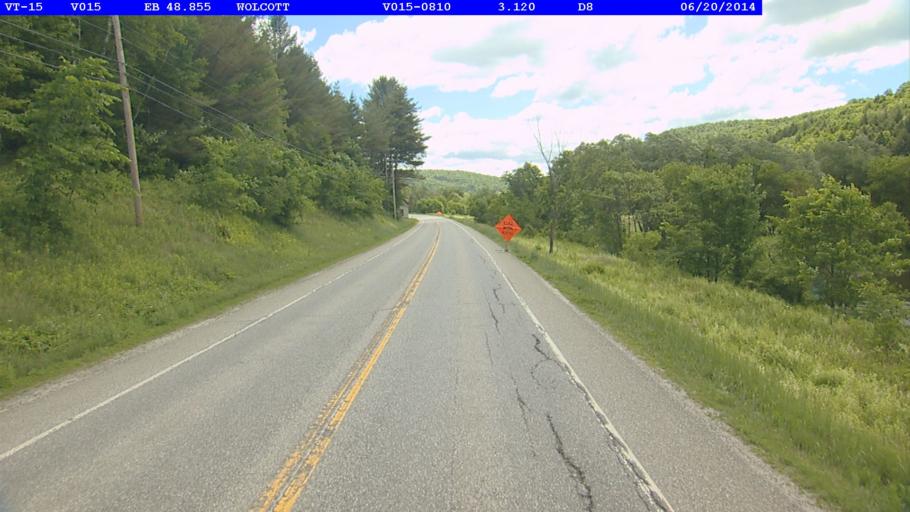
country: US
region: Vermont
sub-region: Lamoille County
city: Morrisville
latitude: 44.5532
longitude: -72.4788
